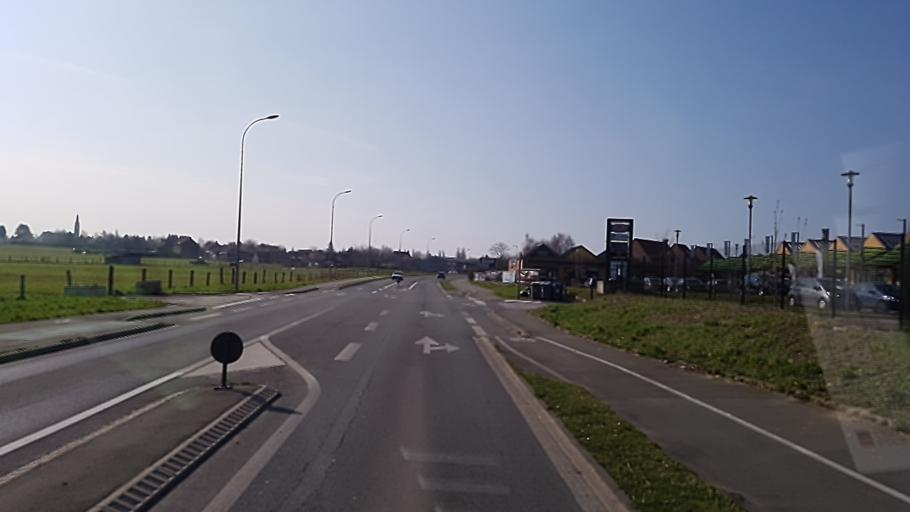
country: FR
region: Nord-Pas-de-Calais
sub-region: Departement du Nord
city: Halluin
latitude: 50.7824
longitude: 3.1396
